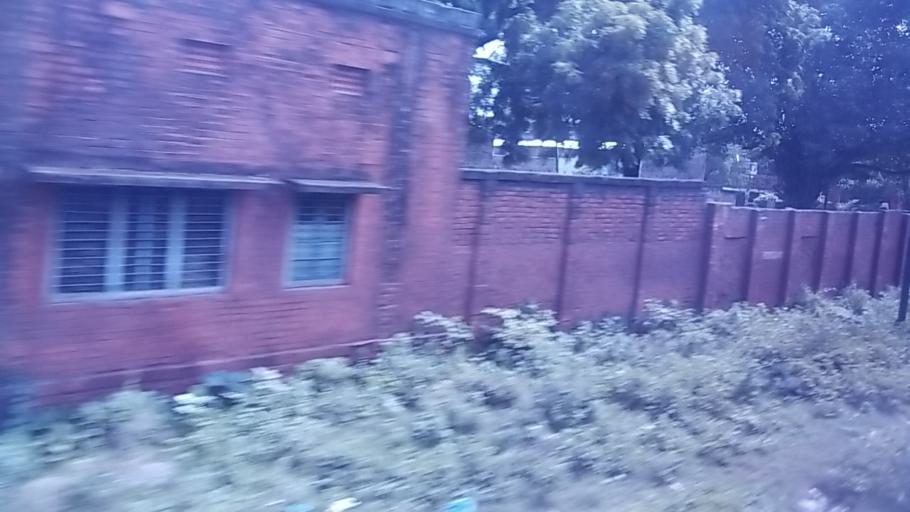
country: IN
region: Uttar Pradesh
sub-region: Allahabad
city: Allahabad
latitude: 25.4430
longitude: 81.8041
